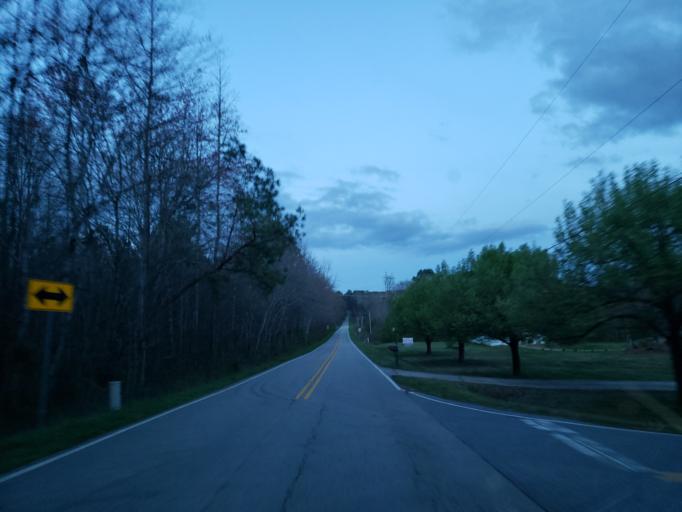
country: US
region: Georgia
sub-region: Paulding County
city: Dallas
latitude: 34.0065
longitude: -84.8969
